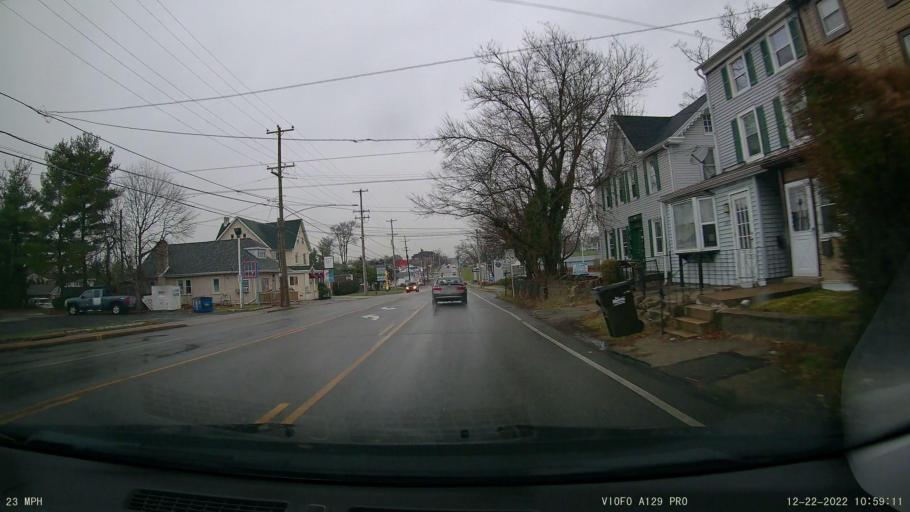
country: US
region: Pennsylvania
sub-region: Montgomery County
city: West Norriton
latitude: 40.1329
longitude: -75.3785
